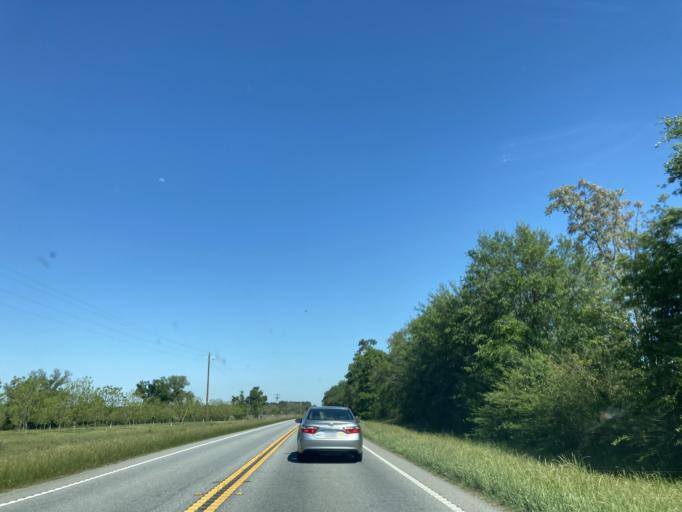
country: US
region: Georgia
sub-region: Miller County
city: Colquitt
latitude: 31.1863
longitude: -84.6312
